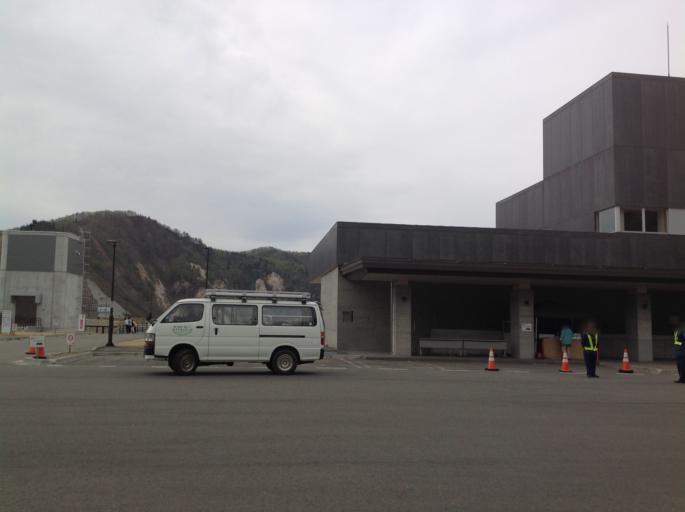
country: JP
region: Iwate
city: Mizusawa
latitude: 39.1253
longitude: 140.9203
